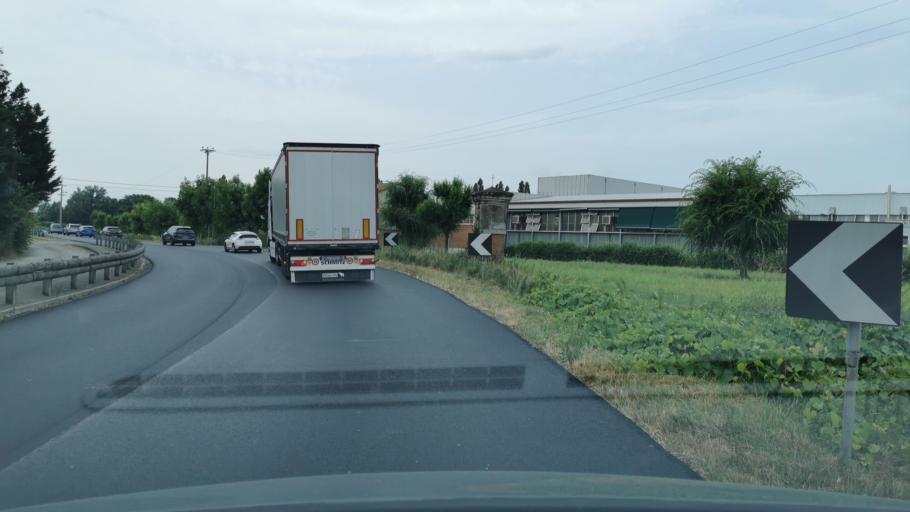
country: IT
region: Emilia-Romagna
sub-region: Provincia di Modena
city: Villanova
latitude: 44.6988
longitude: 10.8920
